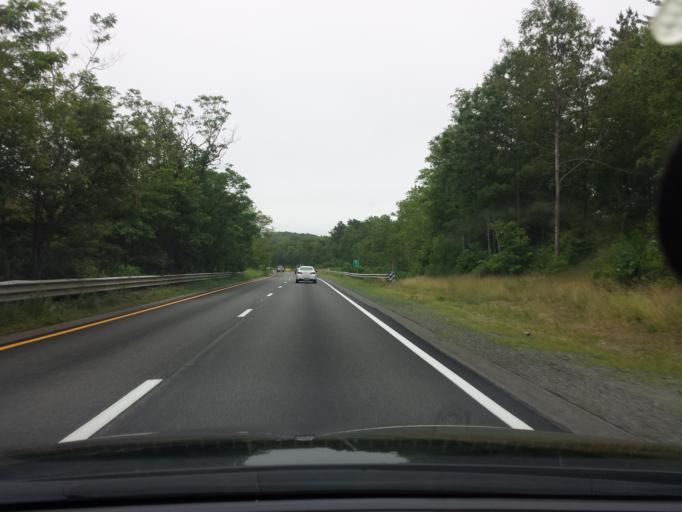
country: US
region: Massachusetts
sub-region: Barnstable County
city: Sandwich
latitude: 41.7486
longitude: -70.5144
